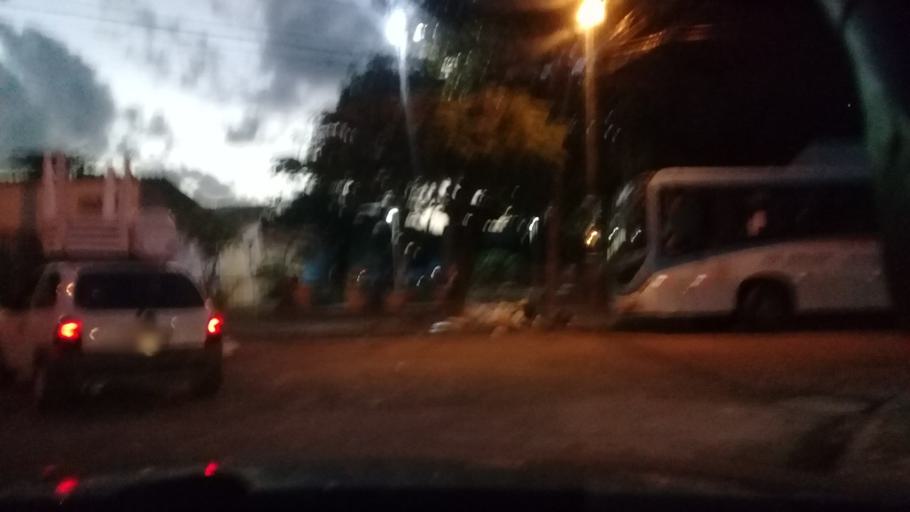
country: BR
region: Pernambuco
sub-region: Recife
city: Recife
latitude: -8.1129
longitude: -34.9241
